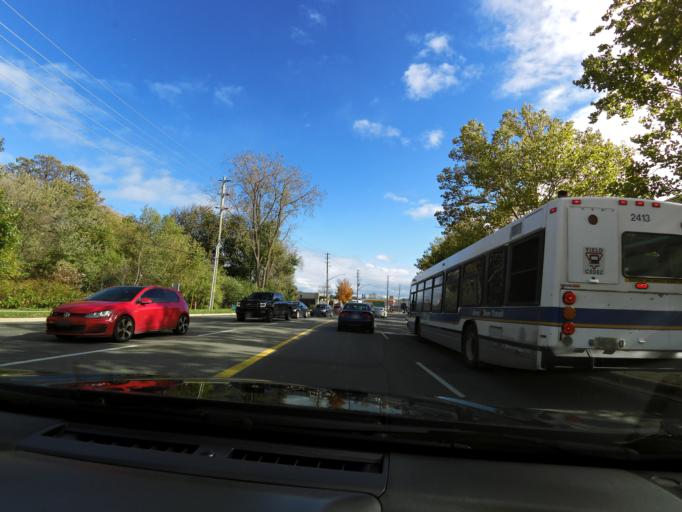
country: CA
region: Ontario
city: Waterloo
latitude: 43.4639
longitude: -80.5407
